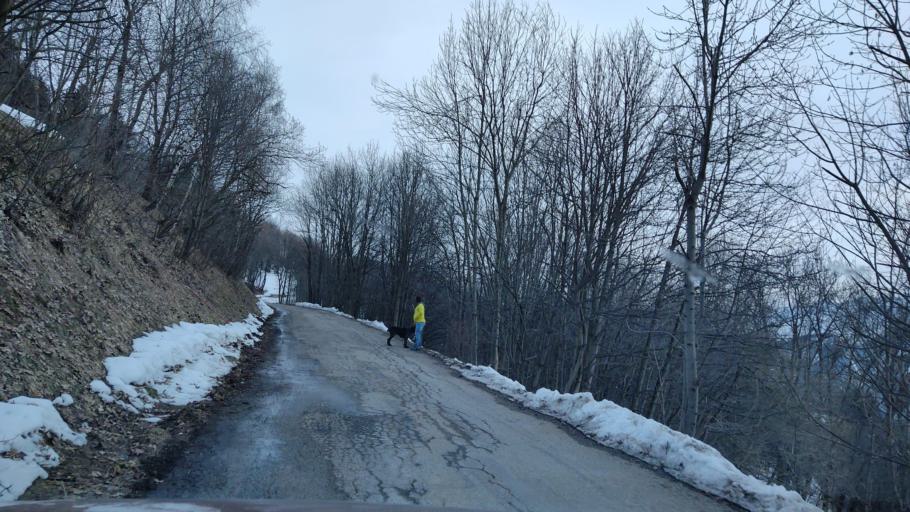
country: FR
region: Rhone-Alpes
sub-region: Departement de la Savoie
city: Saint-Michel-de-Maurienne
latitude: 45.2496
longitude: 6.4731
